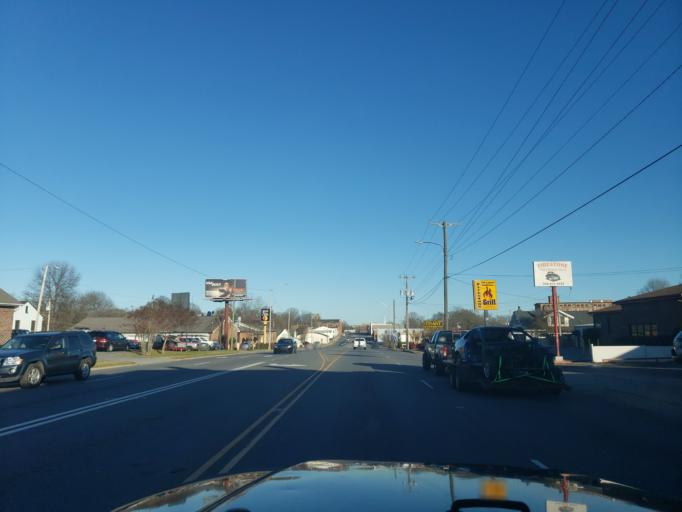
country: US
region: North Carolina
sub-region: Gaston County
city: Gastonia
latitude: 35.2608
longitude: -81.2067
